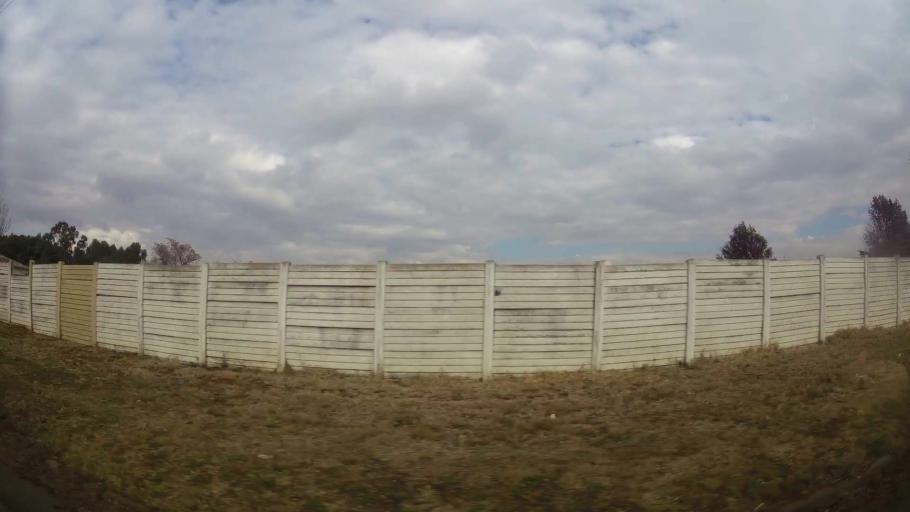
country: ZA
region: Gauteng
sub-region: Sedibeng District Municipality
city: Meyerton
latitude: -26.5976
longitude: 27.9986
